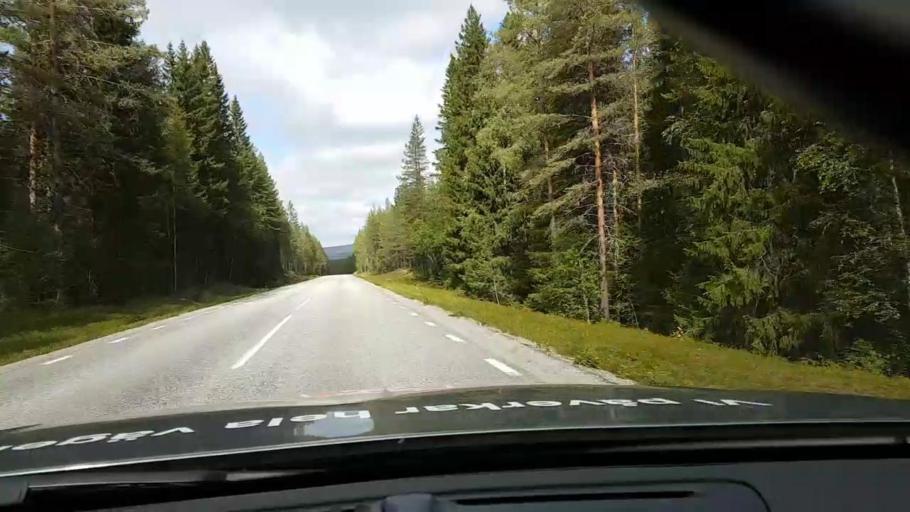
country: SE
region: Vaesternorrland
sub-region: OErnskoeldsviks Kommun
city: Bredbyn
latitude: 63.6974
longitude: 17.7642
